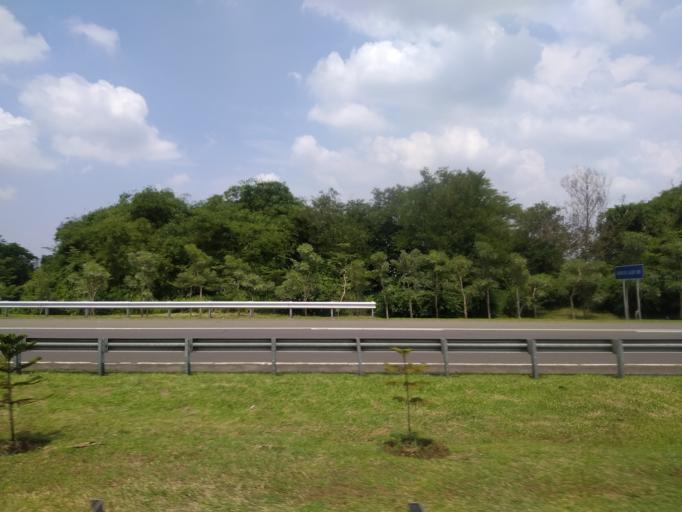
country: ID
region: West Java
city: Bogor
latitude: -6.5964
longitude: 106.8223
